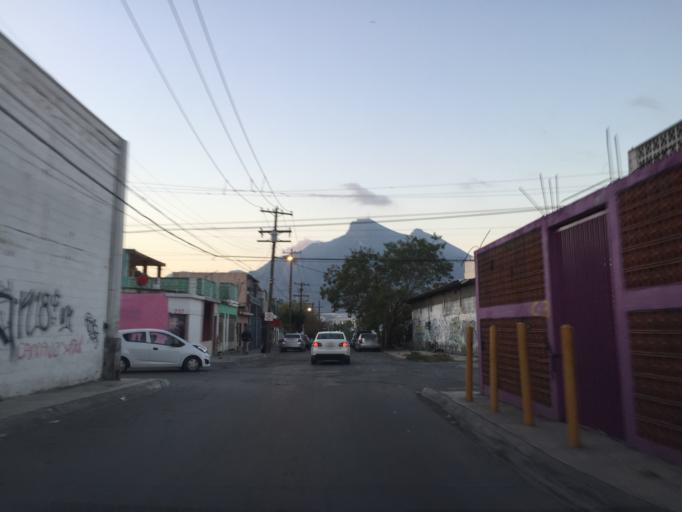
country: MX
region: Nuevo Leon
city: Guadalupe
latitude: 25.6950
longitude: -100.2290
